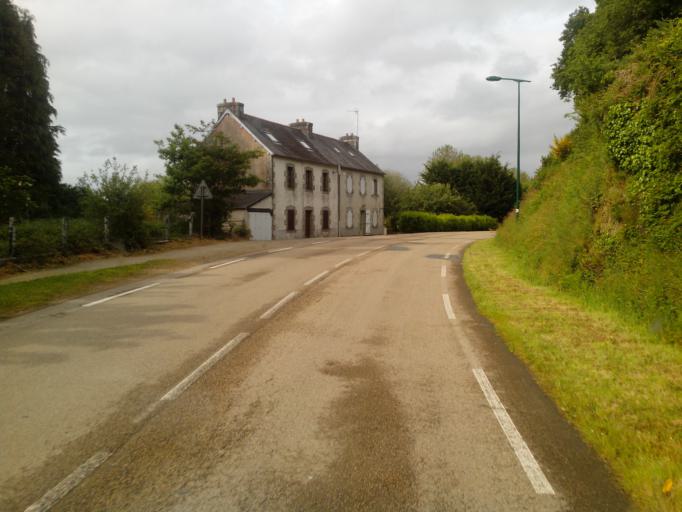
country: FR
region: Brittany
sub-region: Departement du Finistere
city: Huelgoat
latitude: 48.3613
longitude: -3.7547
